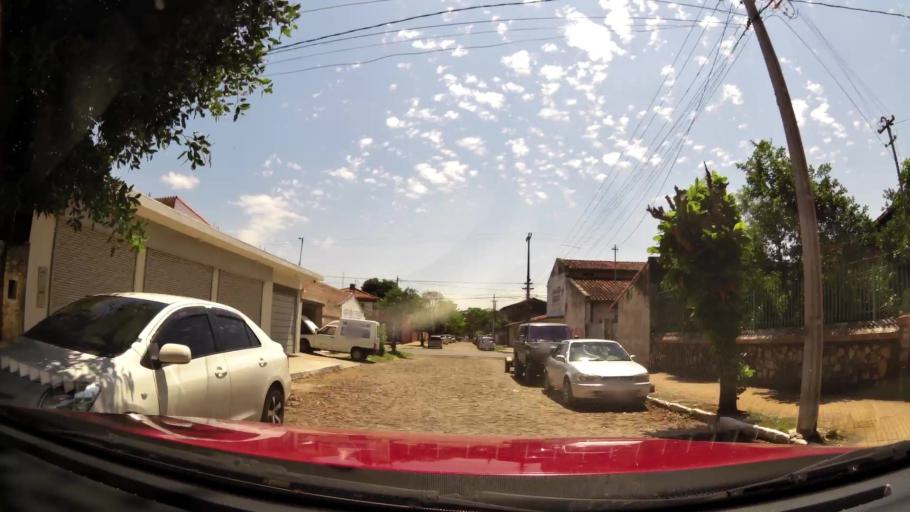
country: PY
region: Central
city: Fernando de la Mora
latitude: -25.3256
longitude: -57.5593
